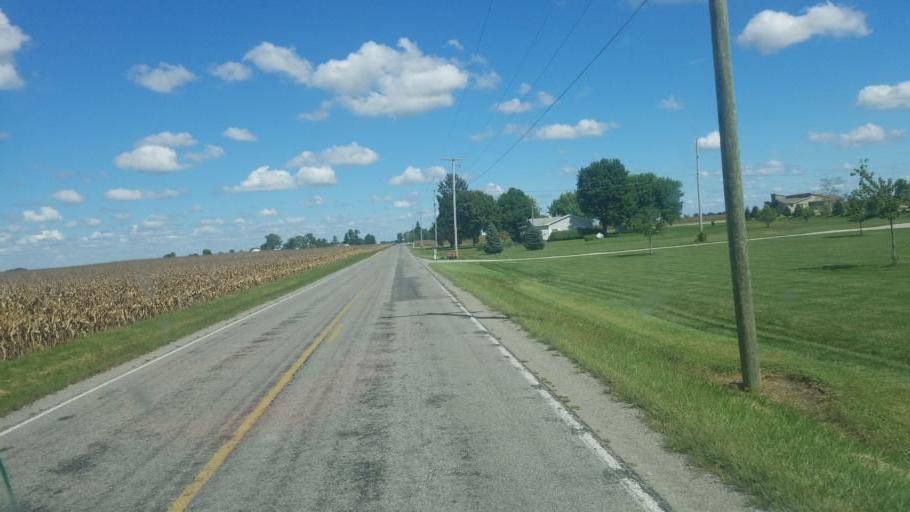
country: US
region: Ohio
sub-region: Madison County
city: Plain City
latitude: 40.0315
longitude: -83.3688
